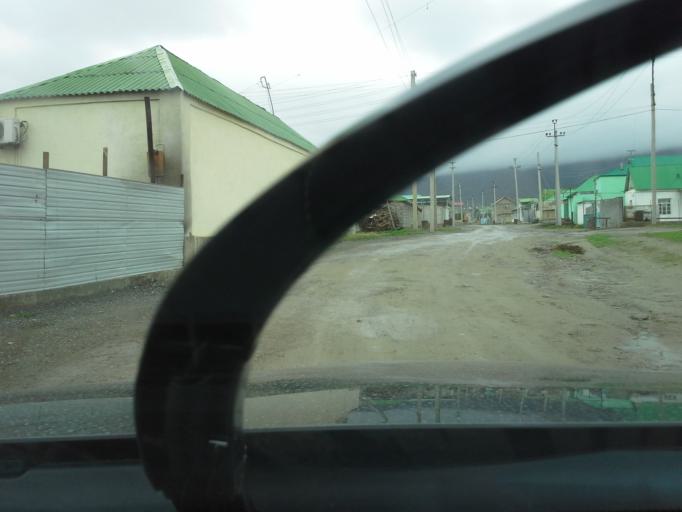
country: TM
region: Ahal
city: Abadan
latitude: 37.9670
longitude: 58.2086
